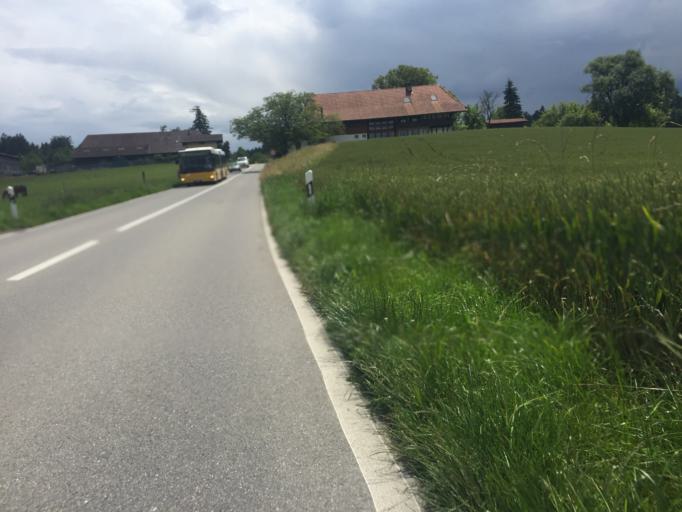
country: CH
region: Bern
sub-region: Bern-Mittelland District
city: Kirchlindach
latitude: 46.9893
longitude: 7.4065
